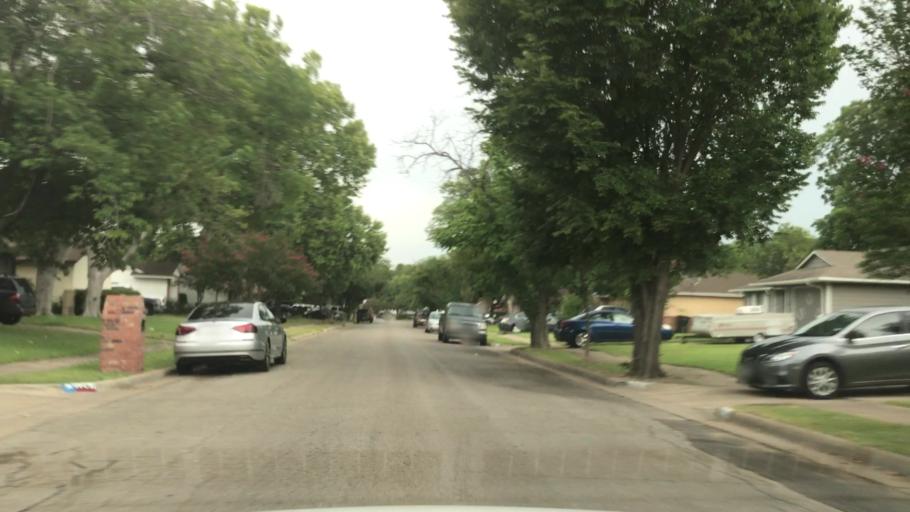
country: US
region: Texas
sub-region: Dallas County
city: Garland
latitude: 32.8736
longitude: -96.6470
